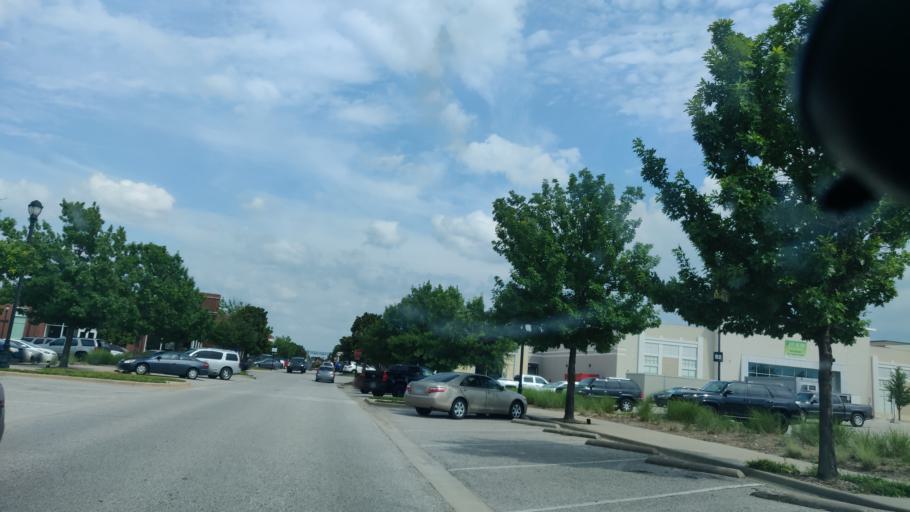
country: US
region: Texas
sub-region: Dallas County
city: Sachse
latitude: 32.9530
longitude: -96.6143
